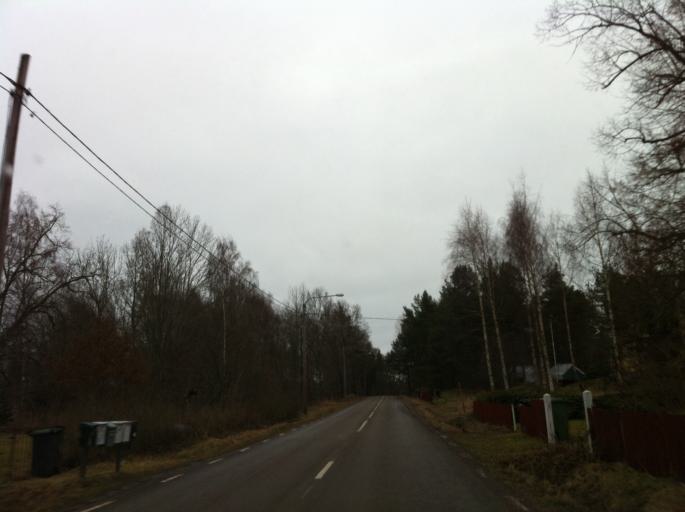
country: SE
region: Kalmar
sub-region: Vasterviks Kommun
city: Vaestervik
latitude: 57.8077
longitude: 16.5930
